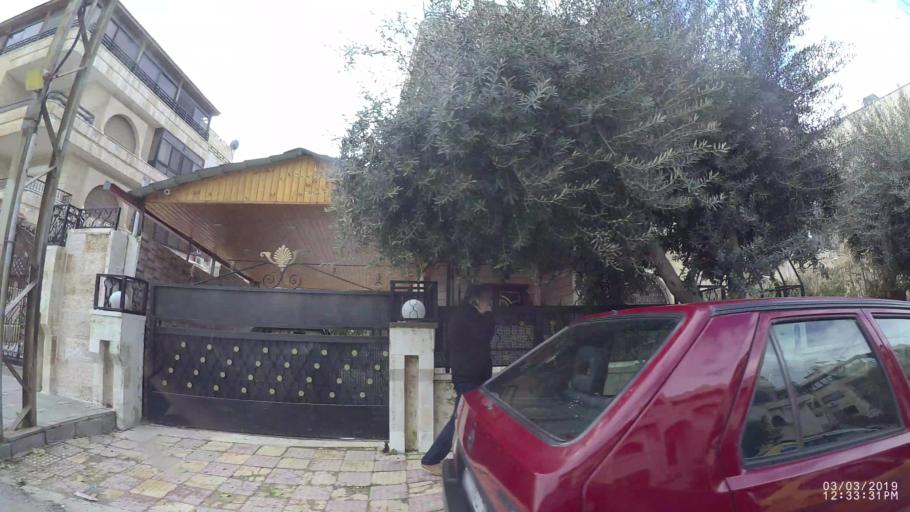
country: JO
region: Amman
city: Amman
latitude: 31.9774
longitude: 35.8984
